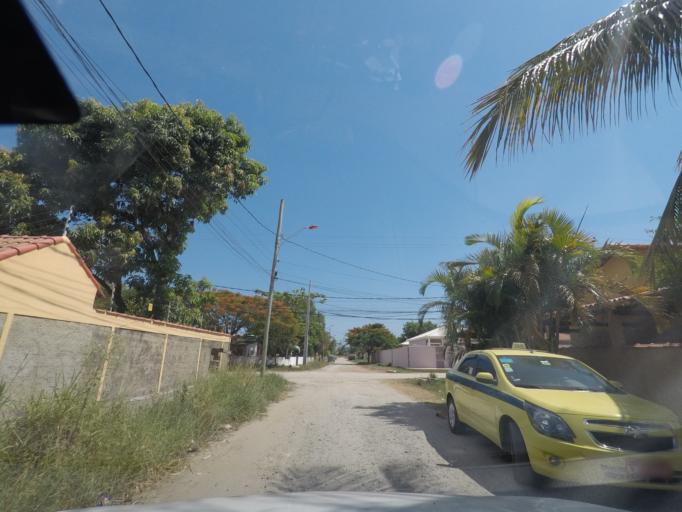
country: BR
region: Rio de Janeiro
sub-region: Marica
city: Marica
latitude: -22.9542
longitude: -42.9629
